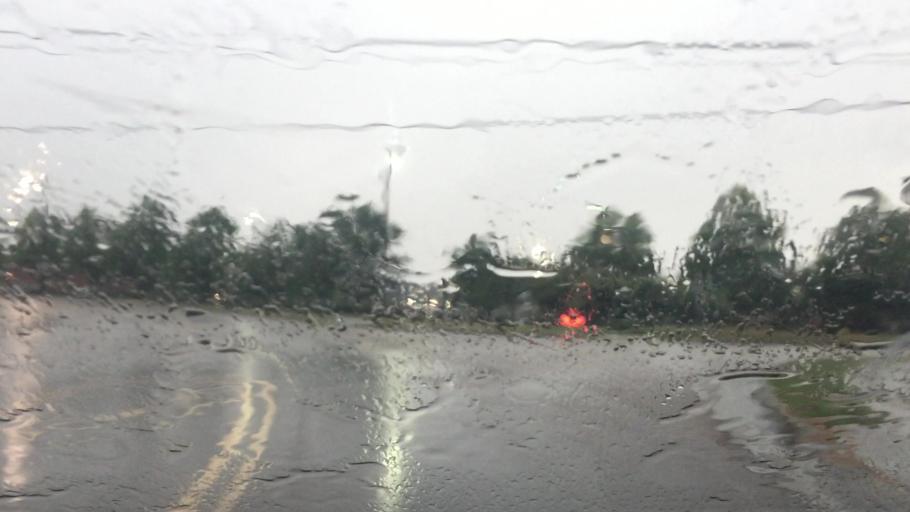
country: US
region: North Carolina
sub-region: Rowan County
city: Salisbury
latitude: 35.6544
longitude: -80.4579
